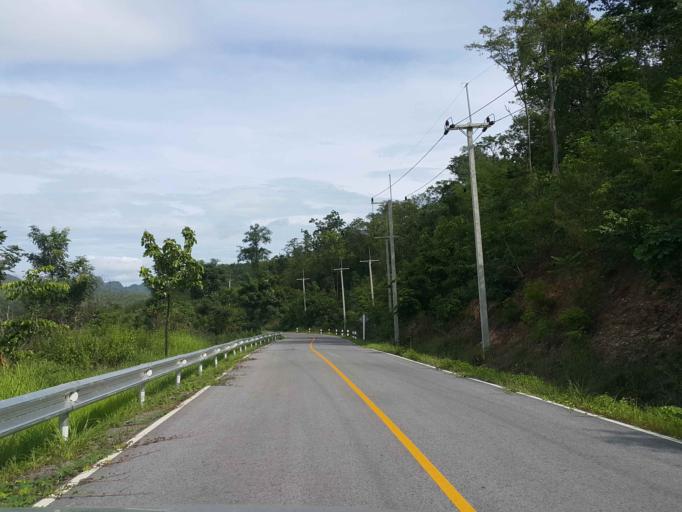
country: TH
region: Sukhothai
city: Thung Saliam
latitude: 17.2403
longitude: 99.4956
